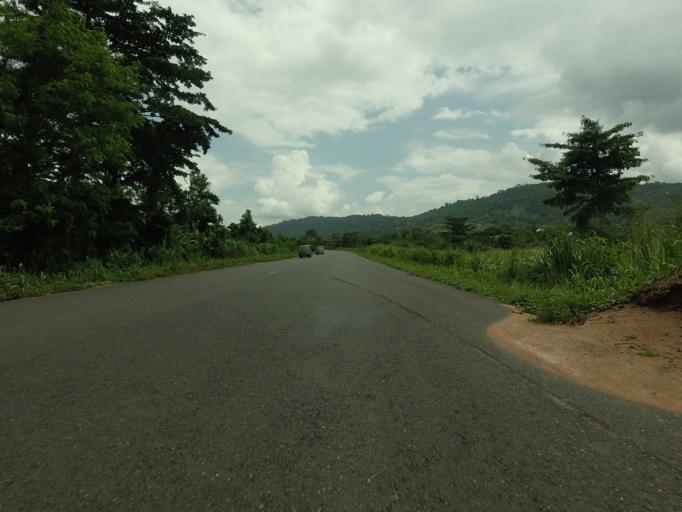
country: GH
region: Volta
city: Ho
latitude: 6.5399
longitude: 0.2378
